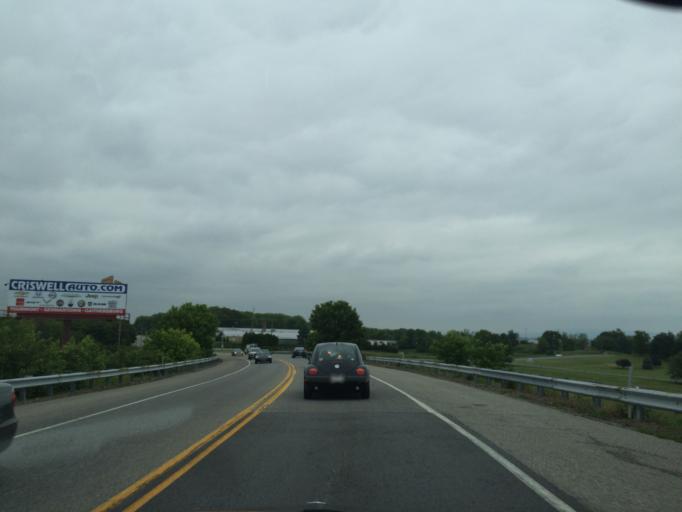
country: US
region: Maryland
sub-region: Washington County
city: Halfway
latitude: 39.6111
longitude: -77.7420
